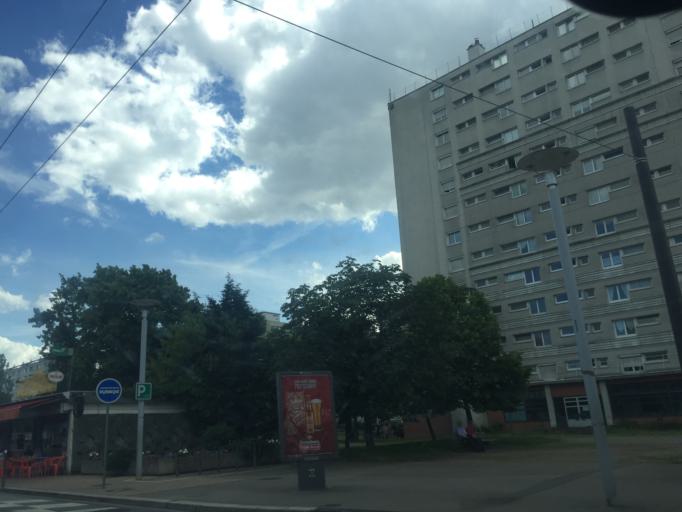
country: FR
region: Rhone-Alpes
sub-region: Departement du Rhone
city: Rillieux-la-Pape
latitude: 45.8145
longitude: 4.8940
